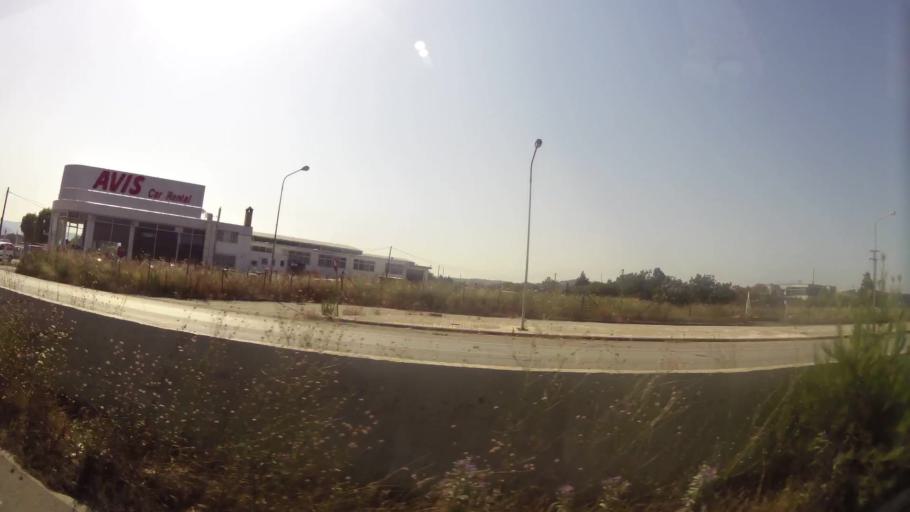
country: GR
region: Central Macedonia
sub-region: Nomos Thessalonikis
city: Neo Rysi
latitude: 40.5090
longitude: 22.9788
